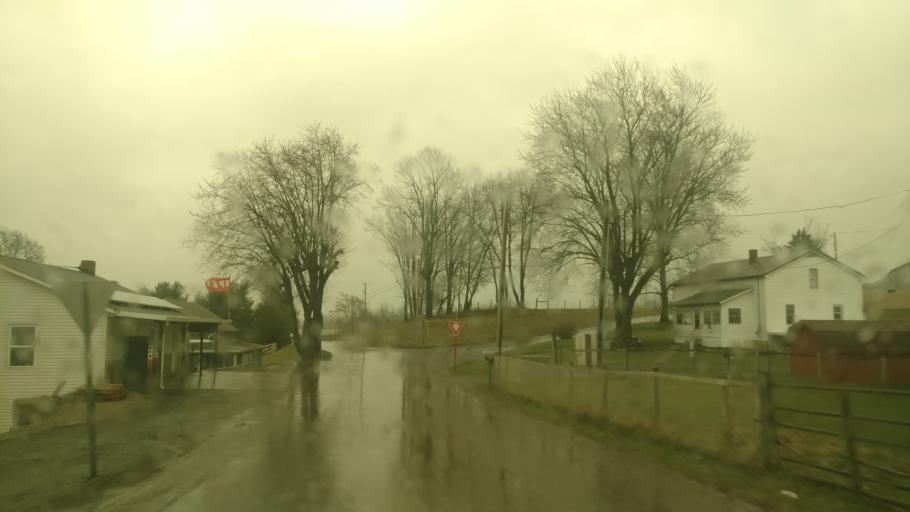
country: US
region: Ohio
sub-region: Holmes County
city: Millersburg
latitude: 40.5206
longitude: -81.8484
